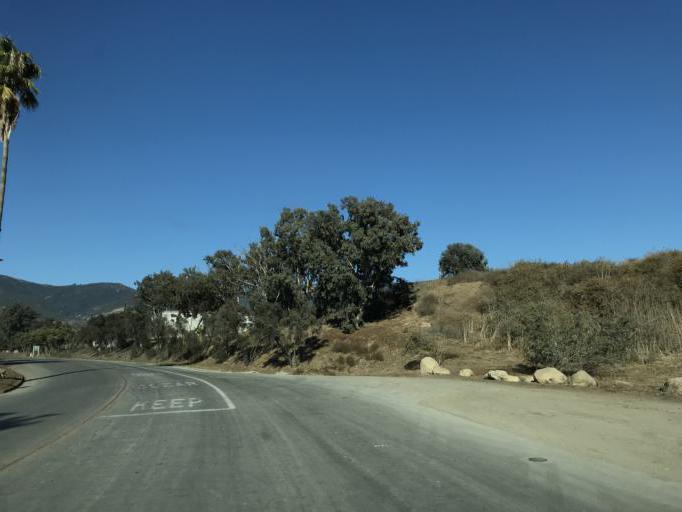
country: US
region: California
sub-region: Santa Barbara County
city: Goleta
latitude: 34.4473
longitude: -119.7736
